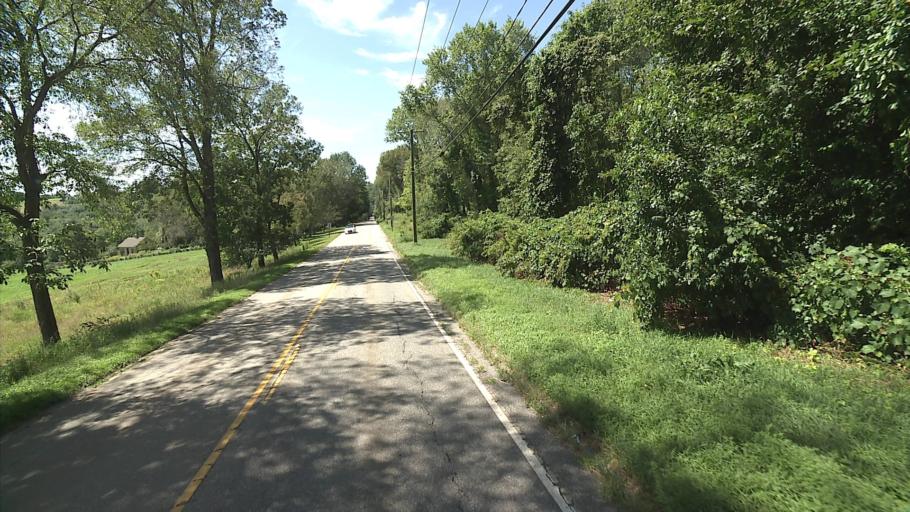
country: US
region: Connecticut
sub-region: Windham County
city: South Woodstock
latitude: 41.8954
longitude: -71.9712
